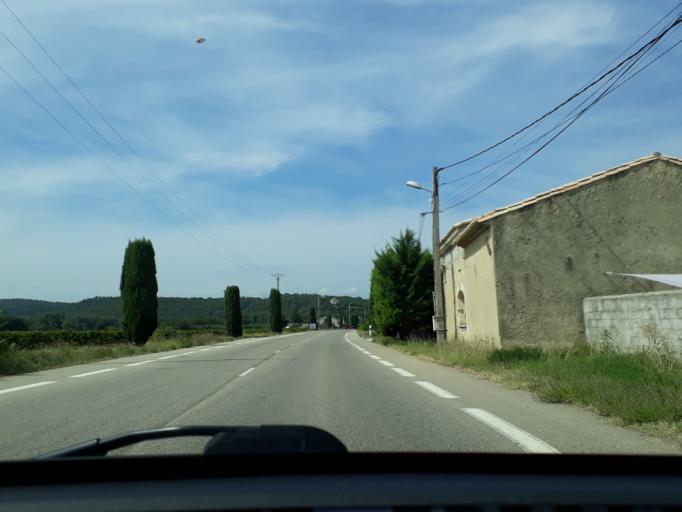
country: FR
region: Rhone-Alpes
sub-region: Departement de la Drome
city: Rochegude
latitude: 44.2727
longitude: 4.7990
